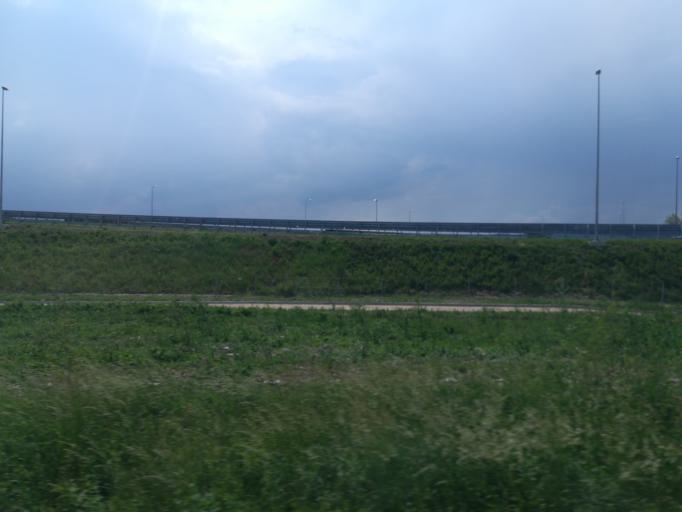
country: IT
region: Veneto
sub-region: Provincia di Vicenza
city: Novoledo
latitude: 45.6621
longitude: 11.5190
